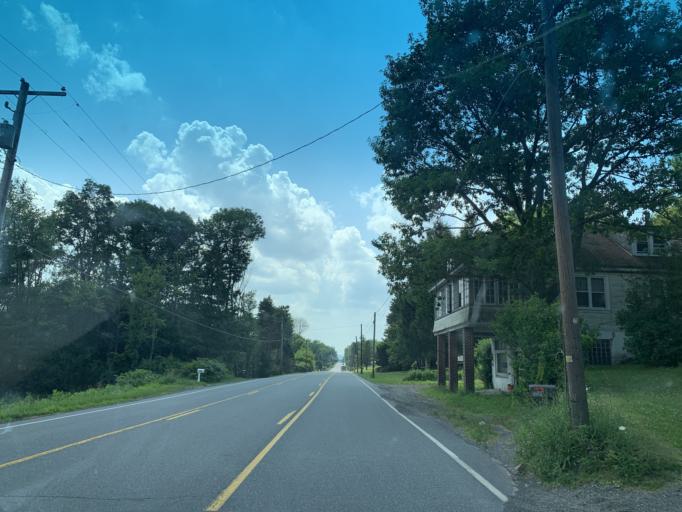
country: US
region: Pennsylvania
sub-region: Schuylkill County
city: Girardville
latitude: 40.7763
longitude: -76.3054
